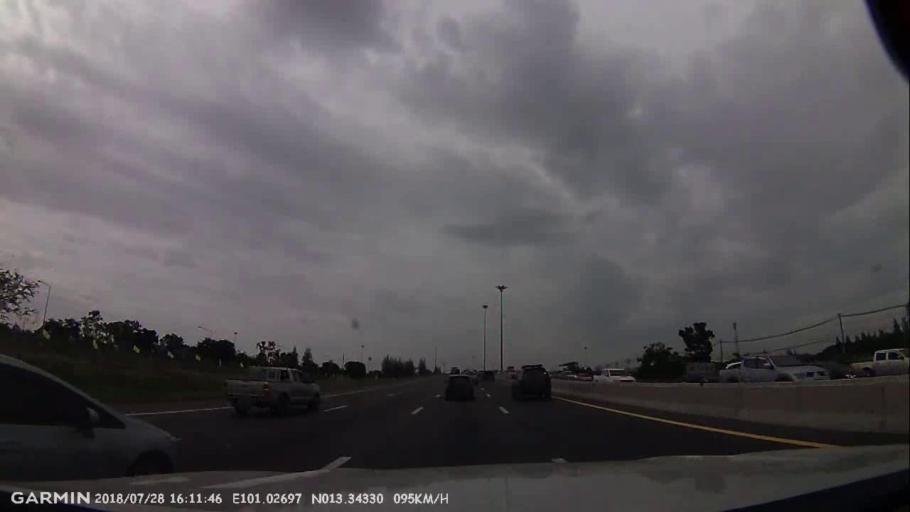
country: TH
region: Chon Buri
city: Chon Buri
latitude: 13.3442
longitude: 101.0270
